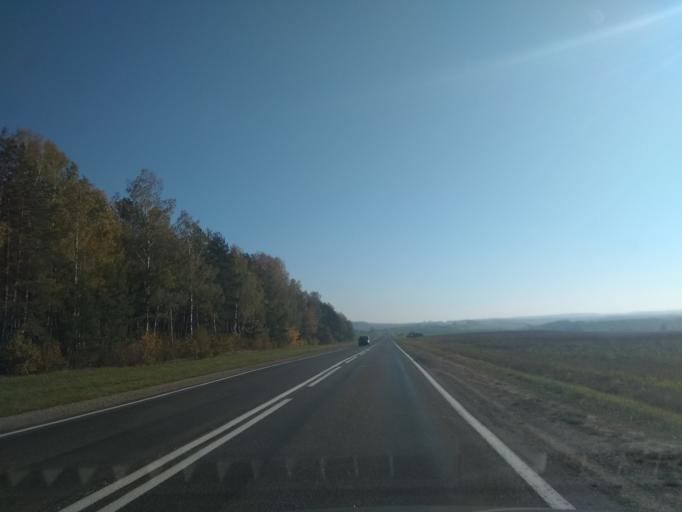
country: BY
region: Grodnenskaya
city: Zel'va
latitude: 53.1310
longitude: 25.0224
